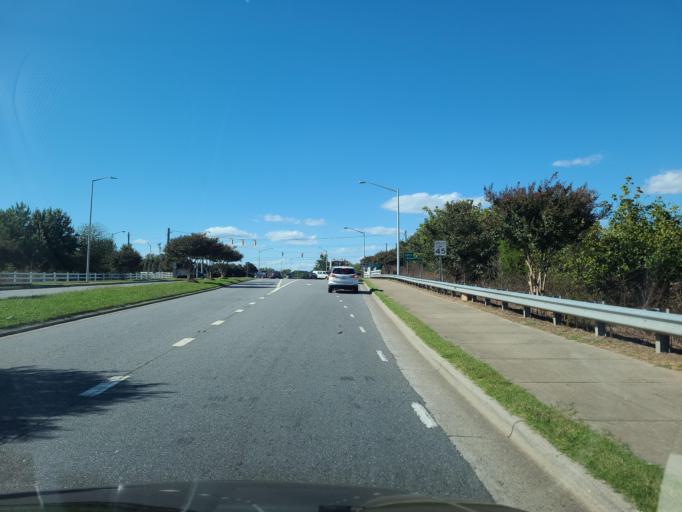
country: US
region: North Carolina
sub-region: Catawba County
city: Conover
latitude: 35.7251
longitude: -81.2064
